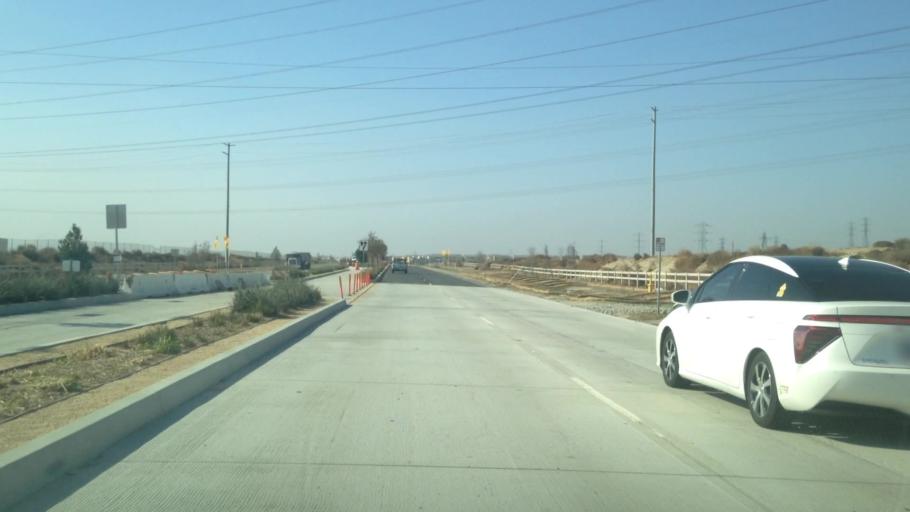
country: US
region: California
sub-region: Riverside County
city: Mira Loma
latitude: 34.0009
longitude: -117.5666
